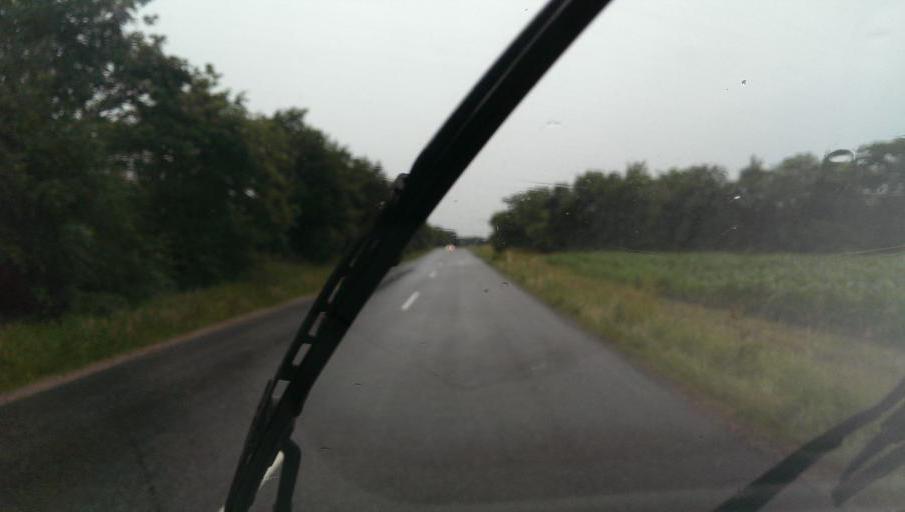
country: DK
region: South Denmark
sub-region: Varde Kommune
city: Oksbol
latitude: 55.6690
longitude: 8.3706
